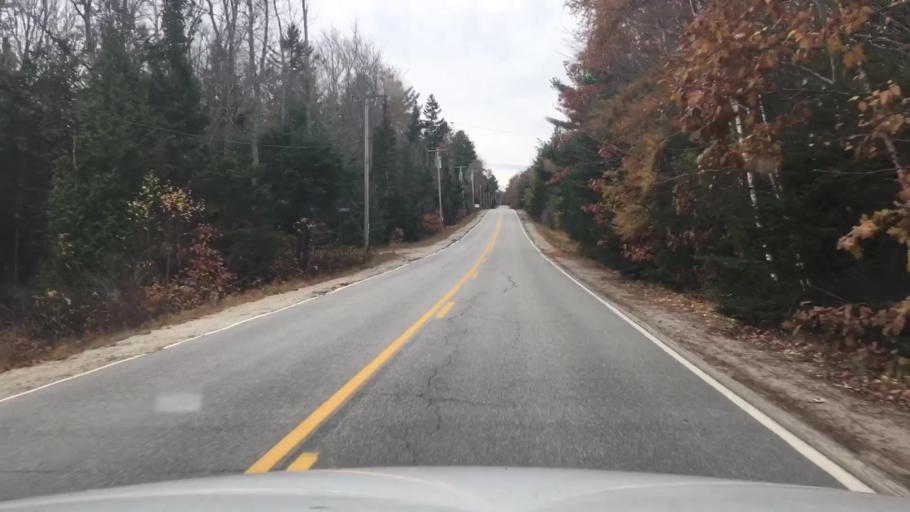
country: US
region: Maine
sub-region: Hancock County
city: Sedgwick
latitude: 44.3147
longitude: -68.5707
